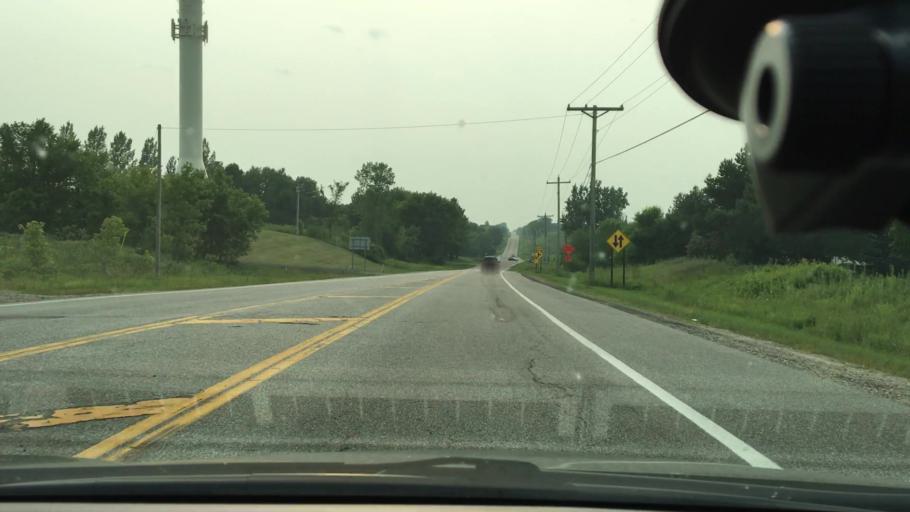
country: US
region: Minnesota
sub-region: Wright County
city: Otsego
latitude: 45.2525
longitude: -93.5598
